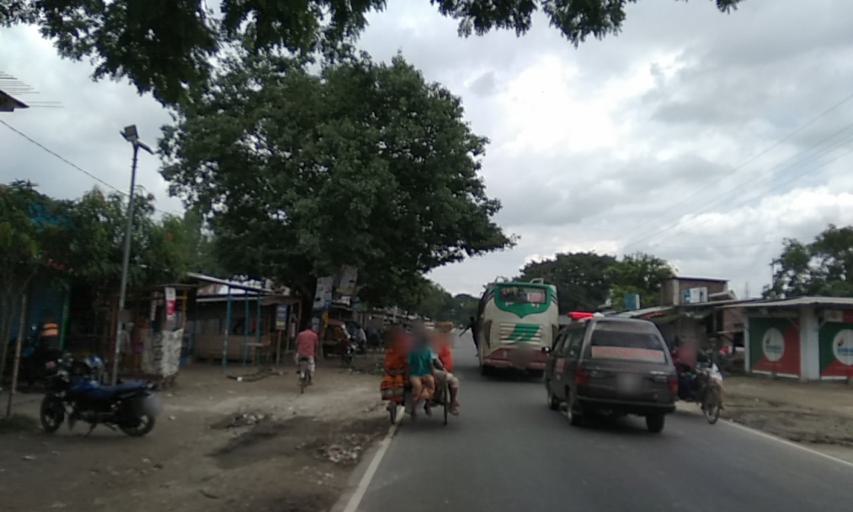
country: BD
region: Rangpur Division
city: Rangpur
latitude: 25.7993
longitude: 89.1917
